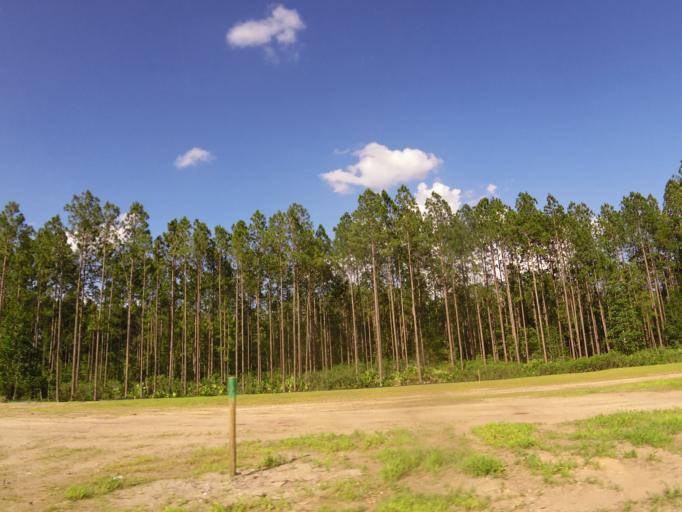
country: US
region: Florida
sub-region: Clay County
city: Green Cove Springs
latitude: 30.0337
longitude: -81.6238
